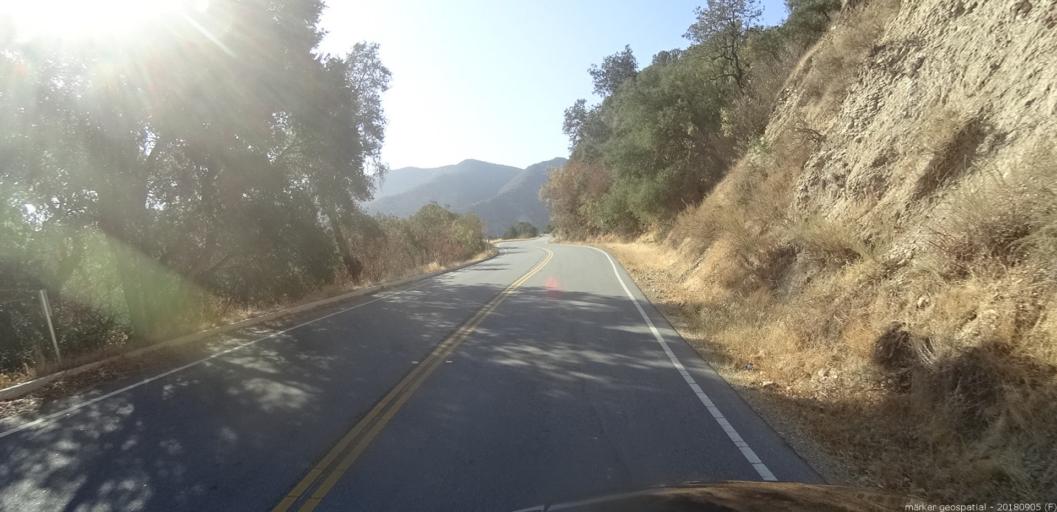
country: US
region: California
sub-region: Monterey County
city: Greenfield
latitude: 36.2531
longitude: -121.4318
